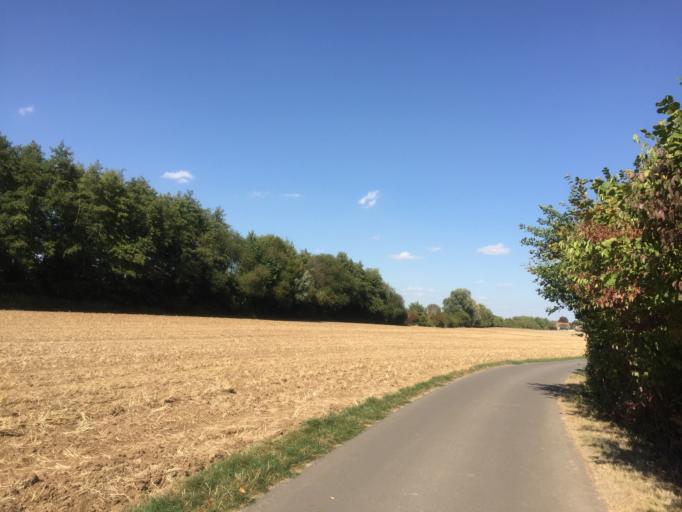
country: DE
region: Hesse
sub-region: Regierungsbezirk Giessen
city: Hungen
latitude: 50.4388
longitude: 8.8987
